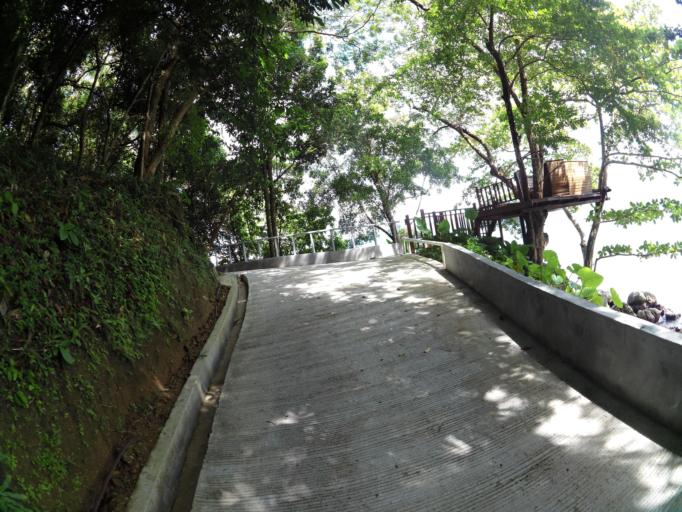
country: TH
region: Phuket
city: Patong
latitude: 7.8879
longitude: 98.2813
